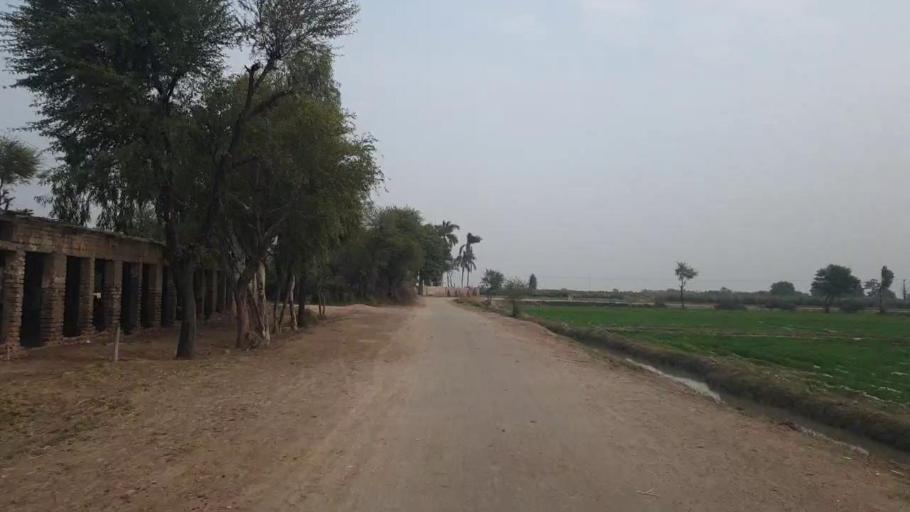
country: PK
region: Sindh
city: Shahdadpur
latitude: 25.9453
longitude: 68.7025
